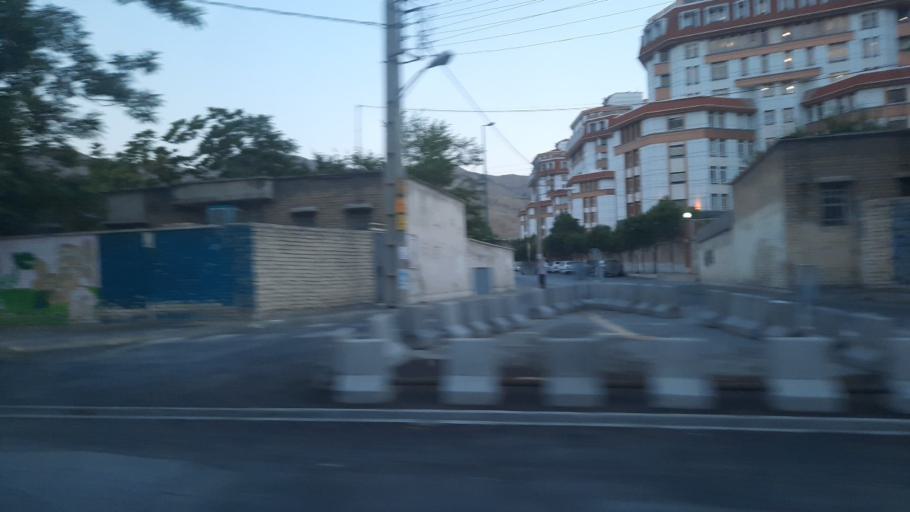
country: IR
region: Markazi
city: Arak
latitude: 34.0747
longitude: 49.7016
